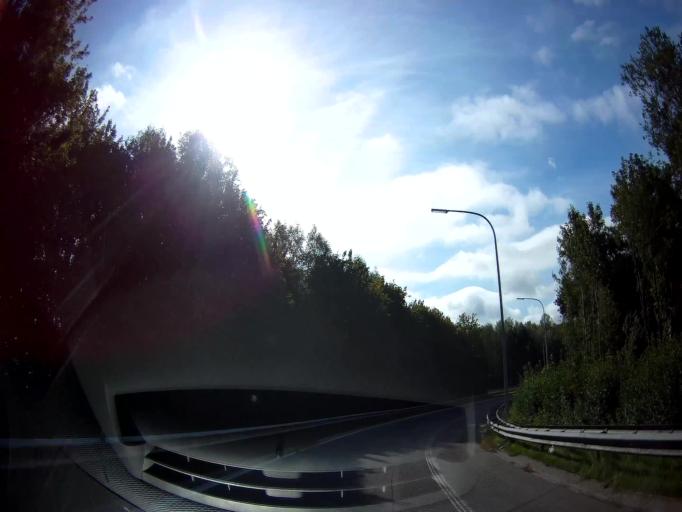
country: BE
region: Wallonia
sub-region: Province de Namur
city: Ciney
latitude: 50.2696
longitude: 5.0369
